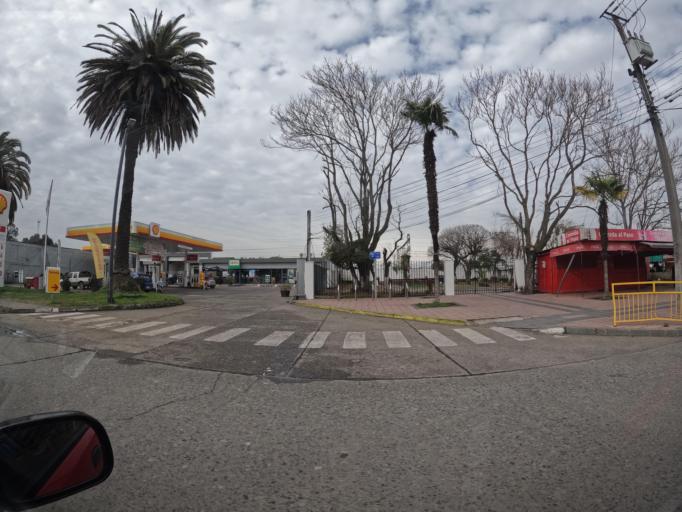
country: CL
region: Maule
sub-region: Provincia de Linares
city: Linares
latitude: -35.8451
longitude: -71.5904
